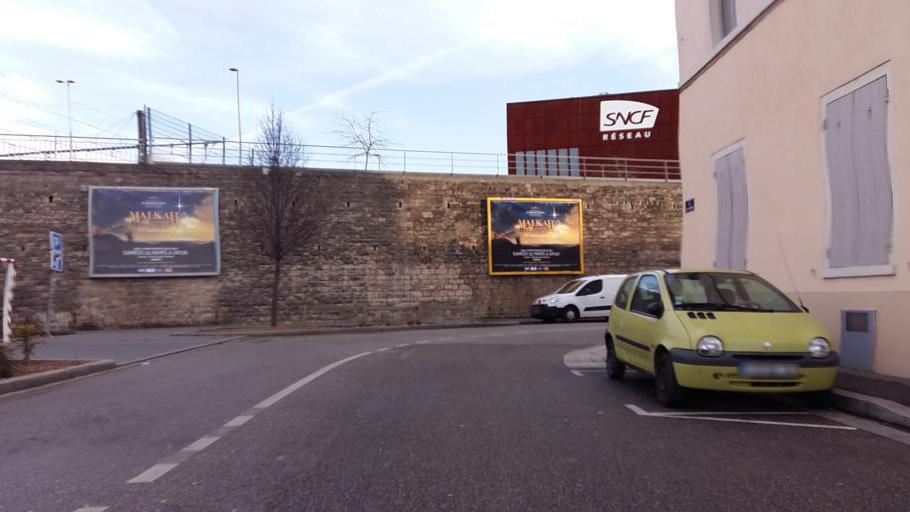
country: FR
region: Rhone-Alpes
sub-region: Departement du Rhone
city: Lyon
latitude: 45.7436
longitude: 4.8412
